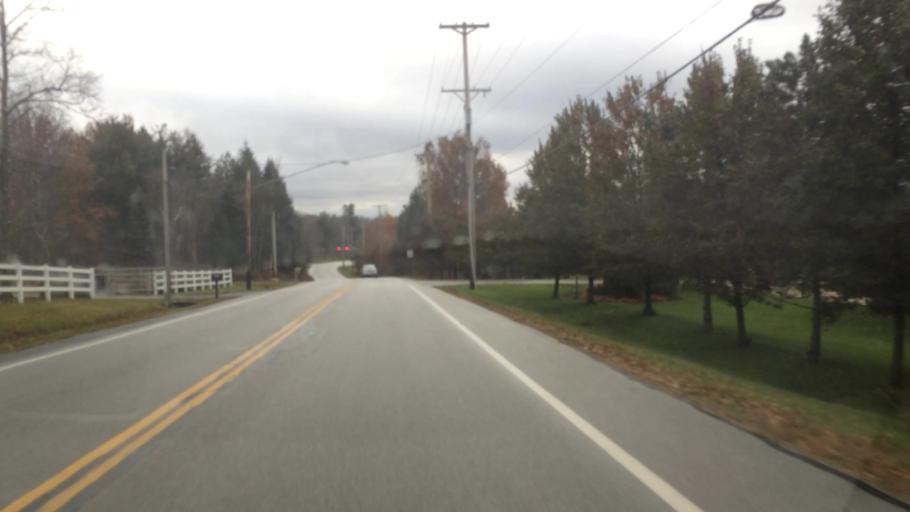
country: US
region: Ohio
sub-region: Summit County
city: Hudson
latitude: 41.2061
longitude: -81.4114
